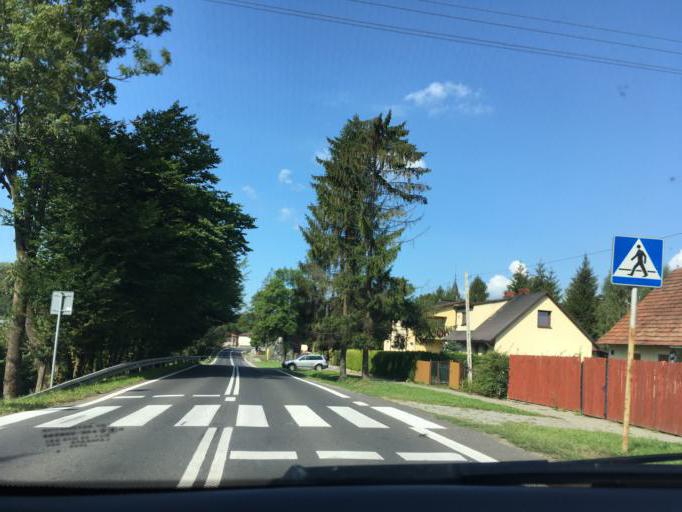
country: PL
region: Subcarpathian Voivodeship
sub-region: Powiat leski
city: Olszanica
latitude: 49.4751
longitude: 22.4509
